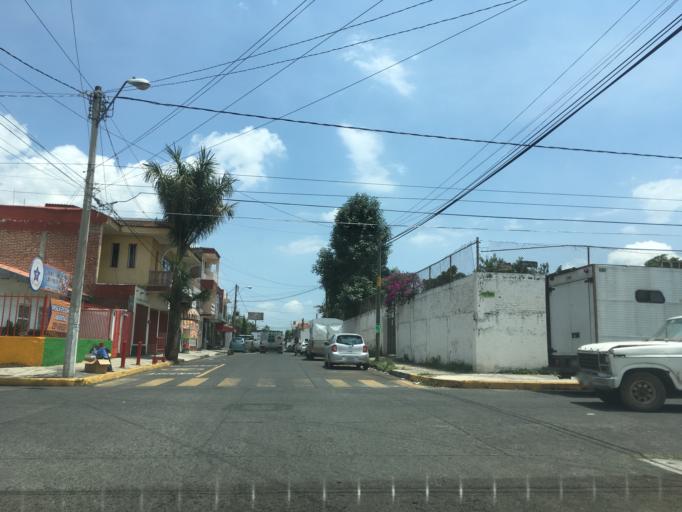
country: MX
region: Michoacan
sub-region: Uruapan
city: Uruapan
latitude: 19.4120
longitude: -102.0546
